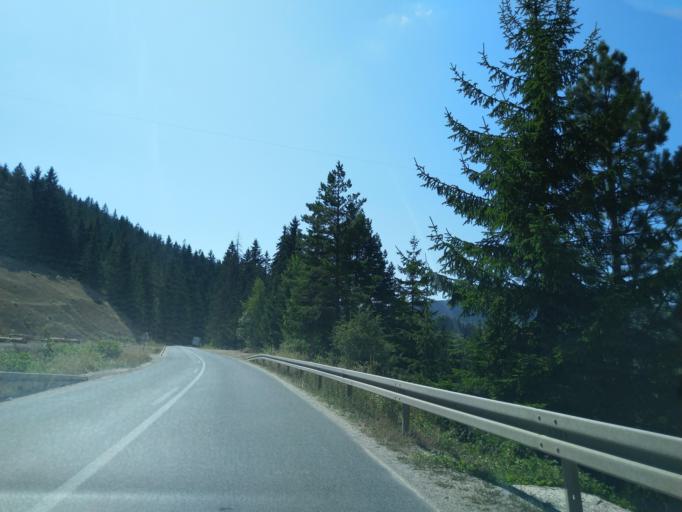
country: RS
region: Central Serbia
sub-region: Zlatiborski Okrug
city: Nova Varos
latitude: 43.4383
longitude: 19.8225
